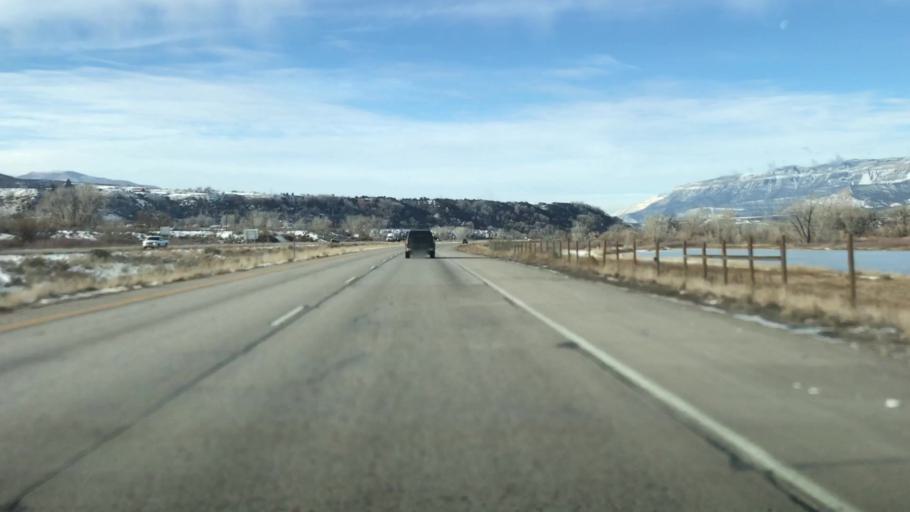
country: US
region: Colorado
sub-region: Garfield County
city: Rifle
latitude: 39.5215
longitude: -107.7869
